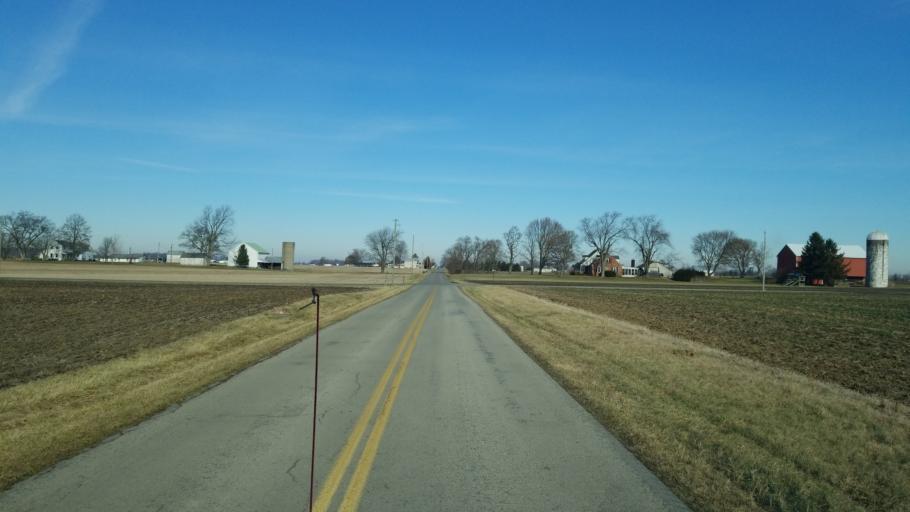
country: US
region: Ohio
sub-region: Putnam County
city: Pandora
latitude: 40.9188
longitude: -83.9377
